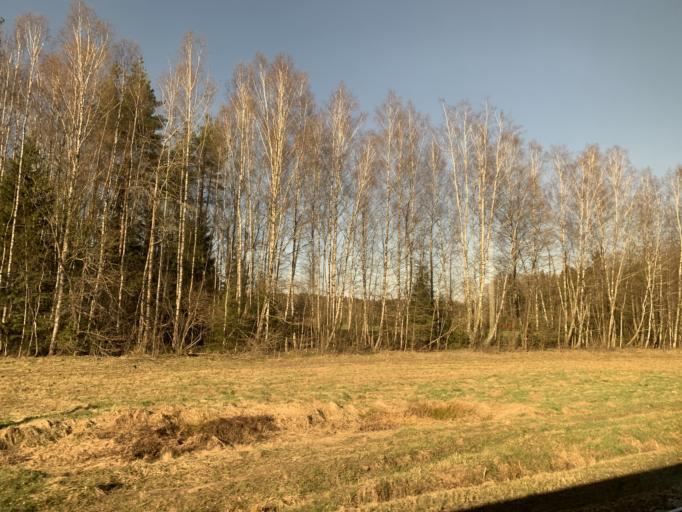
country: BY
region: Grodnenskaya
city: Smarhon'
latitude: 54.4848
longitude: 26.3226
